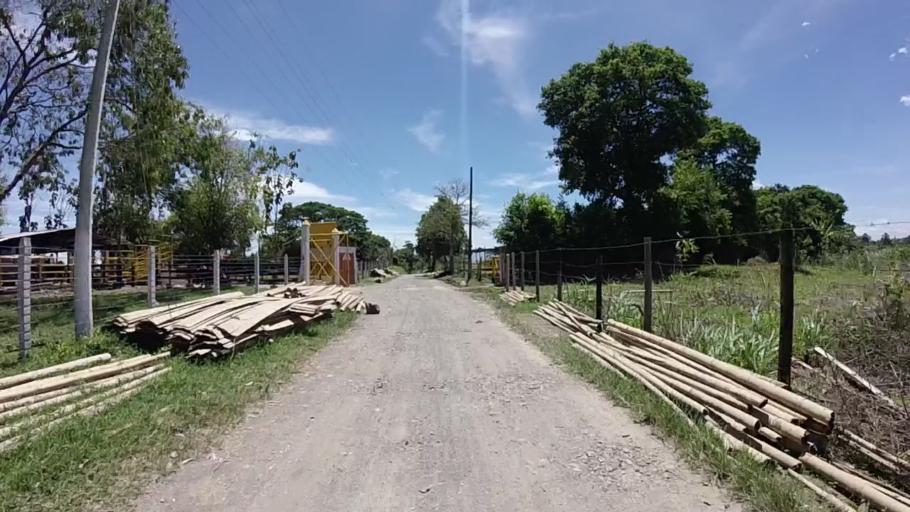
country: CO
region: Valle del Cauca
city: Ulloa
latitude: 4.7150
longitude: -75.7733
